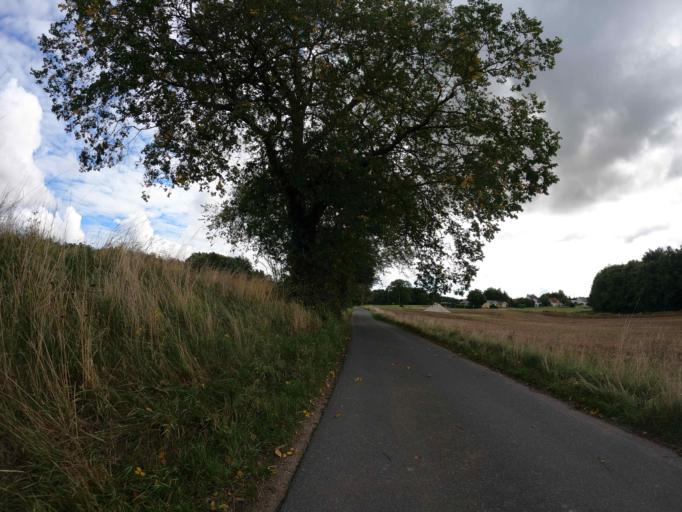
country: DE
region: Mecklenburg-Vorpommern
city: Samtens
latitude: 54.3584
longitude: 13.3346
